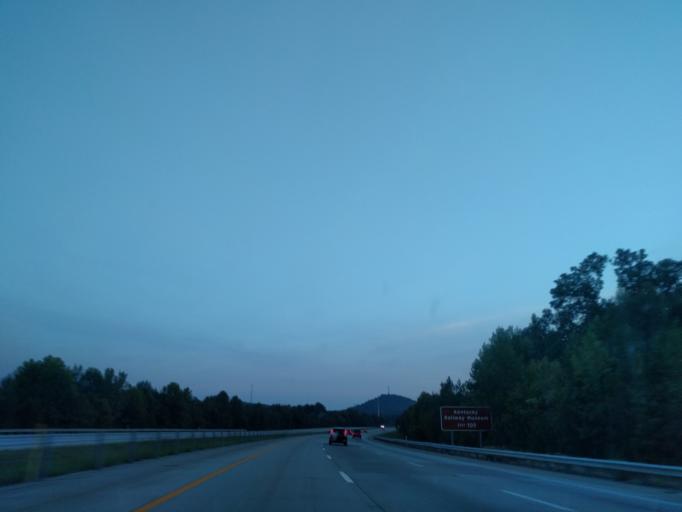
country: US
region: Kentucky
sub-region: Bullitt County
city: Lebanon Junction
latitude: 37.8575
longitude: -85.7084
